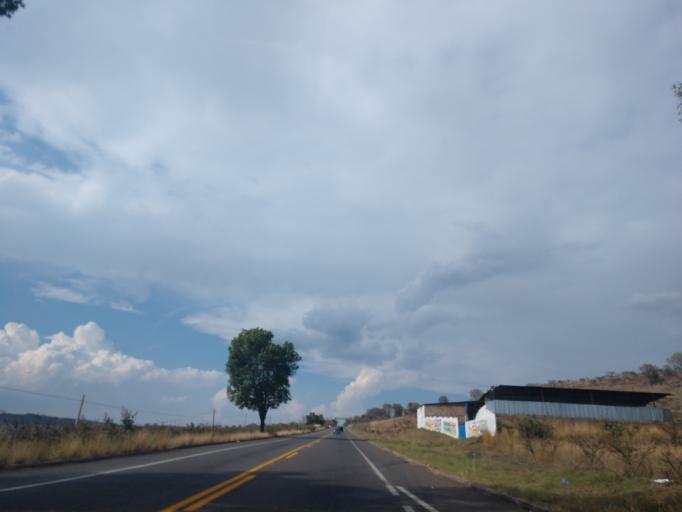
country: MX
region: Jalisco
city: La Manzanilla de la Paz
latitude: 20.0600
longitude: -103.1719
